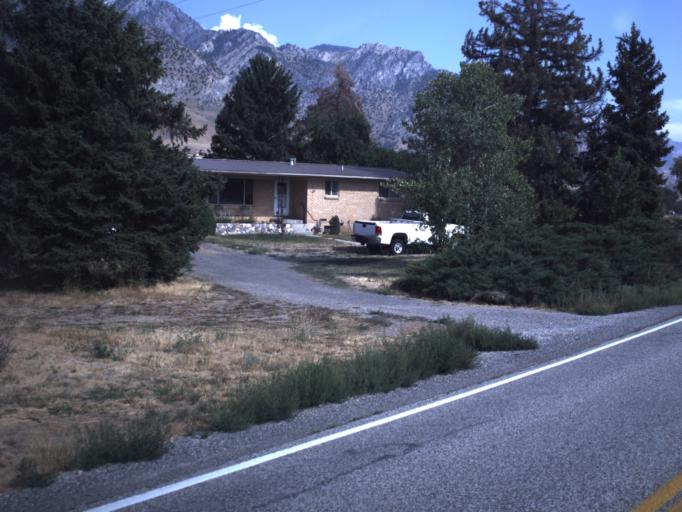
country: US
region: Utah
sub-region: Box Elder County
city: Honeyville
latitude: 41.6457
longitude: -112.0844
